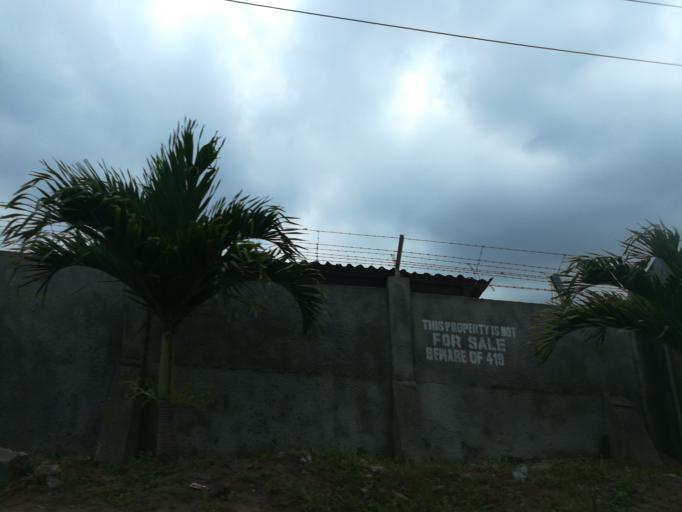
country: NG
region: Lagos
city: Agege
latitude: 6.6237
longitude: 3.3448
